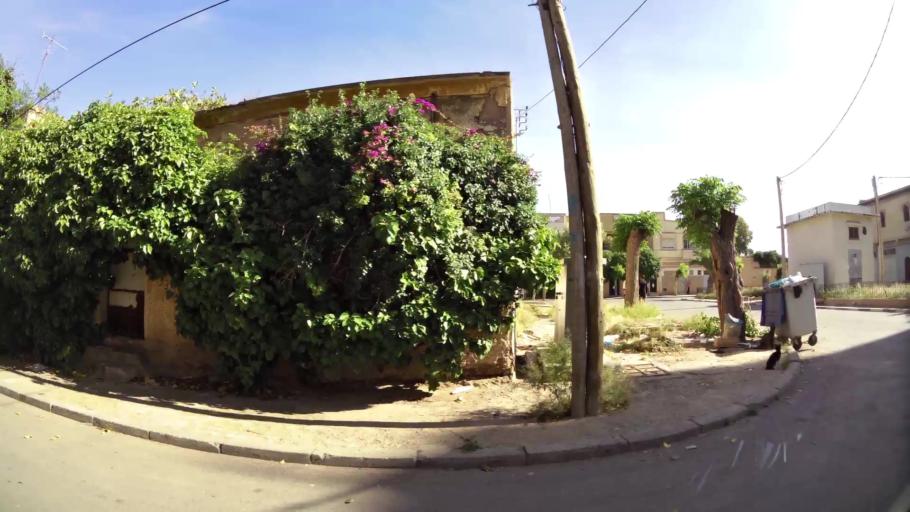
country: MA
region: Oriental
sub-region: Oujda-Angad
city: Oujda
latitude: 34.6707
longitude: -1.9135
